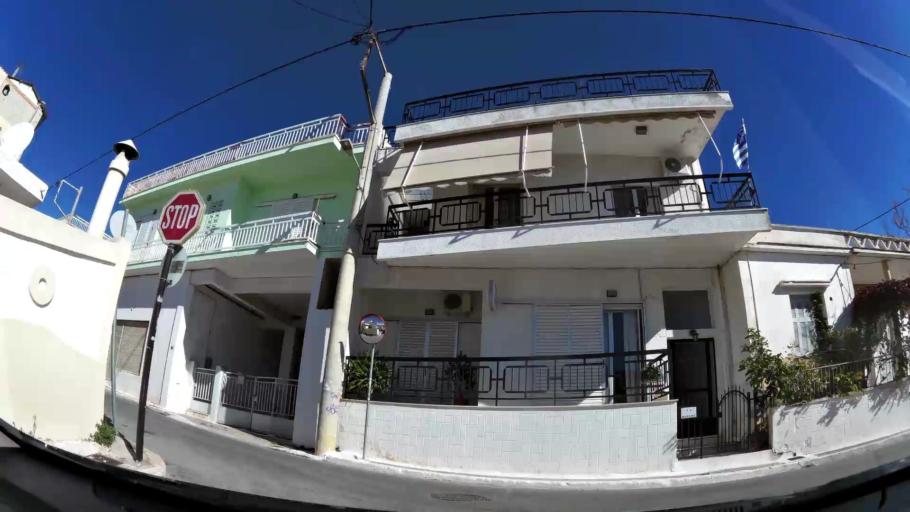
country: GR
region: Attica
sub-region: Nomarchia Anatolikis Attikis
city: Koropi
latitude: 37.9001
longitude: 23.8757
